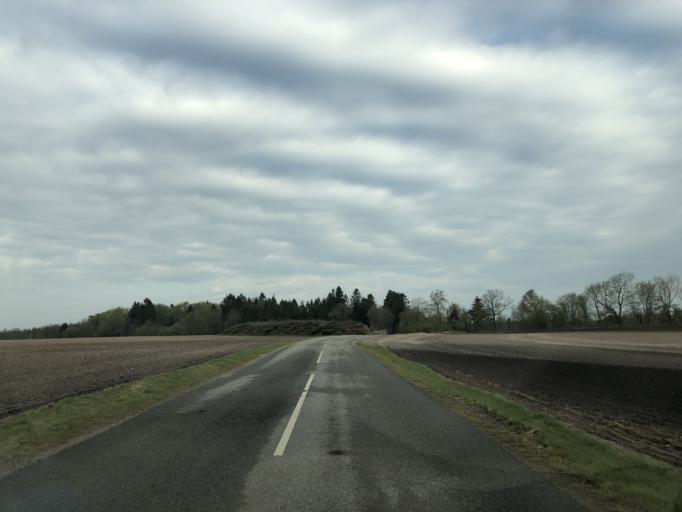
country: DK
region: Central Jutland
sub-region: Holstebro Kommune
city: Holstebro
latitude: 56.3128
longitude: 8.5264
